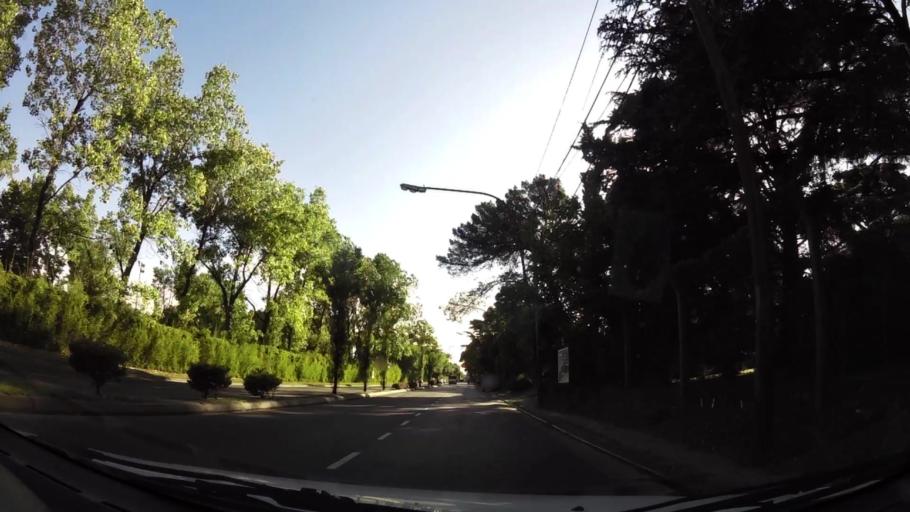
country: AR
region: Buenos Aires
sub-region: Partido de San Isidro
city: San Isidro
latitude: -34.4880
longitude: -58.5393
